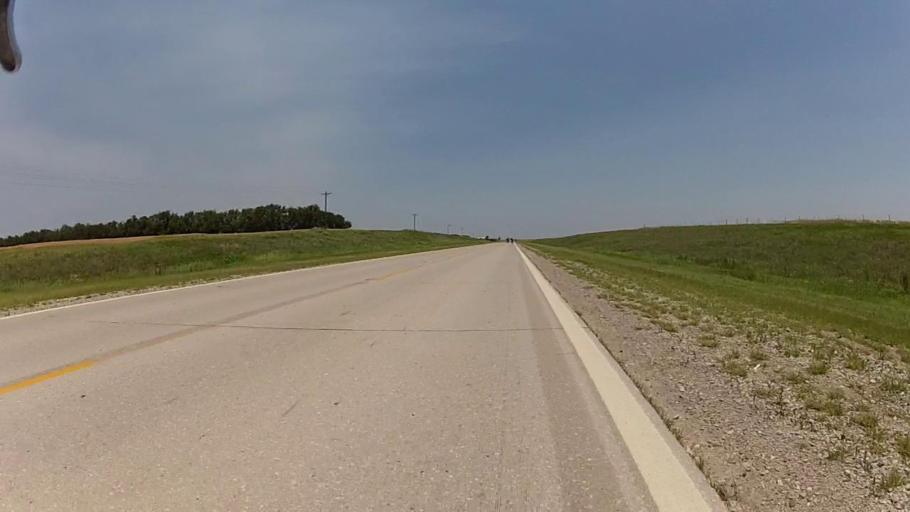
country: US
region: Kansas
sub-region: Sumner County
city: Wellington
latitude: 37.0569
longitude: -97.3211
